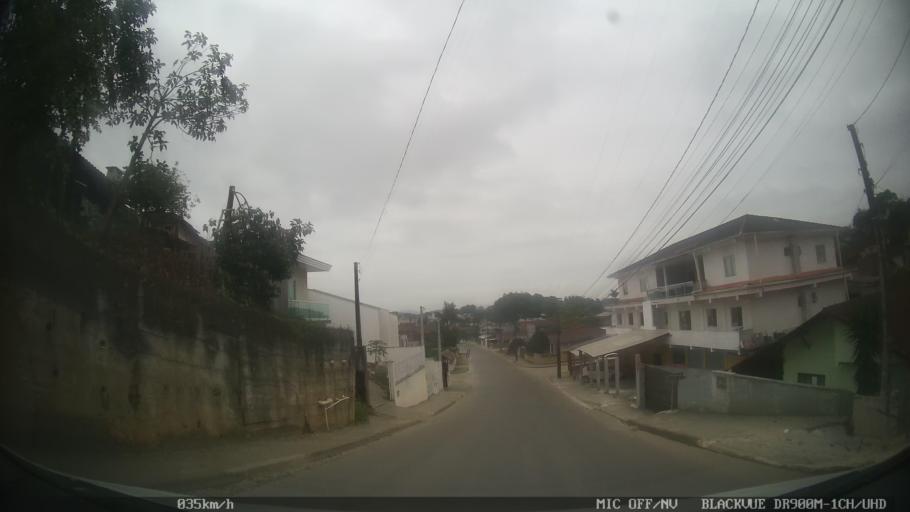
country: BR
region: Santa Catarina
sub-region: Joinville
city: Joinville
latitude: -26.3492
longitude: -48.8259
